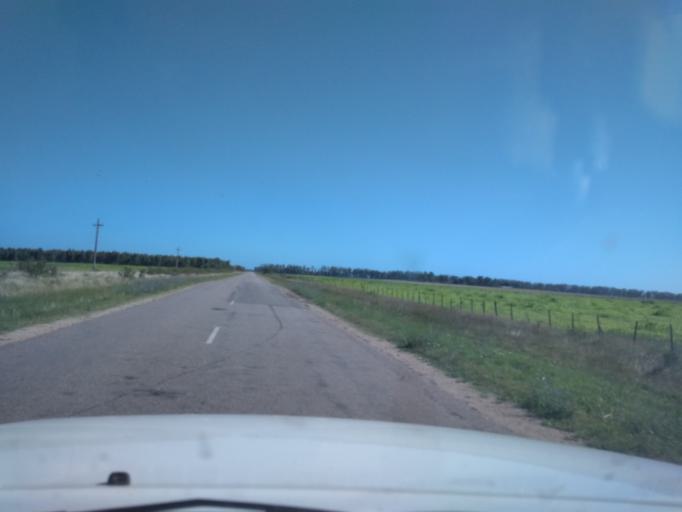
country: UY
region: Canelones
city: San Ramon
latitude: -34.1524
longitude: -55.9462
